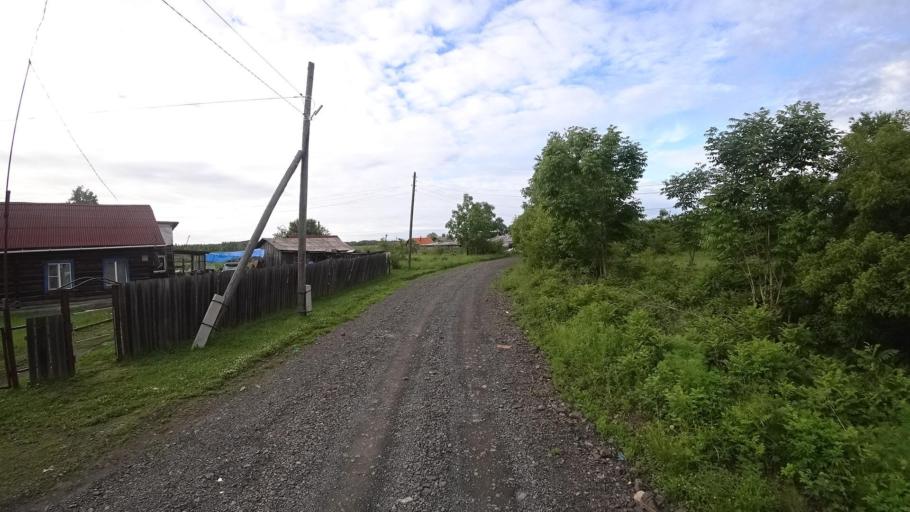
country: RU
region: Khabarovsk Krai
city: Amursk
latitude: 49.8906
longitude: 136.1298
